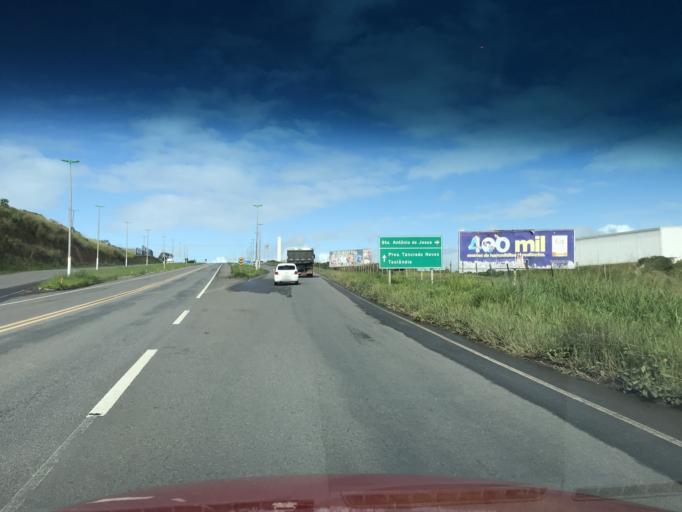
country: BR
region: Bahia
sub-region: Santo Antonio De Jesus
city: Santo Antonio de Jesus
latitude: -12.9608
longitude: -39.2707
